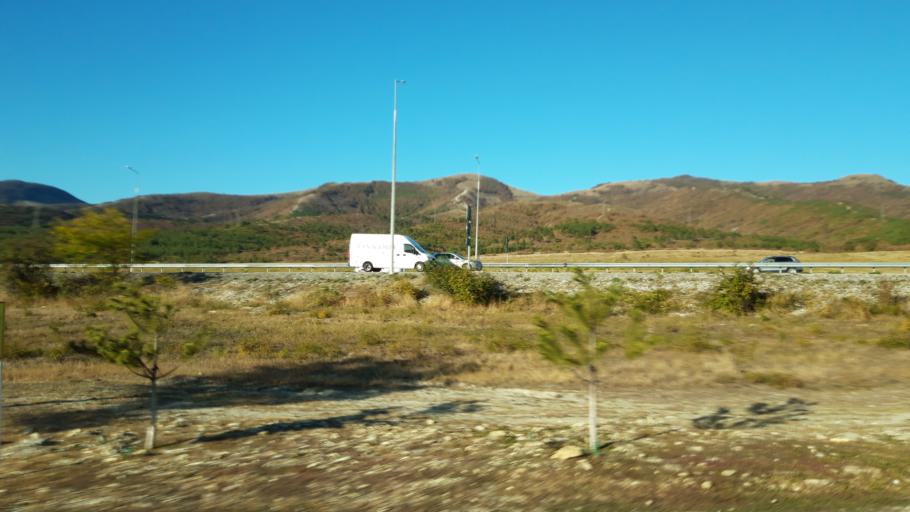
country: RU
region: Krasnodarskiy
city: Kabardinka
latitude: 44.6450
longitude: 37.9643
